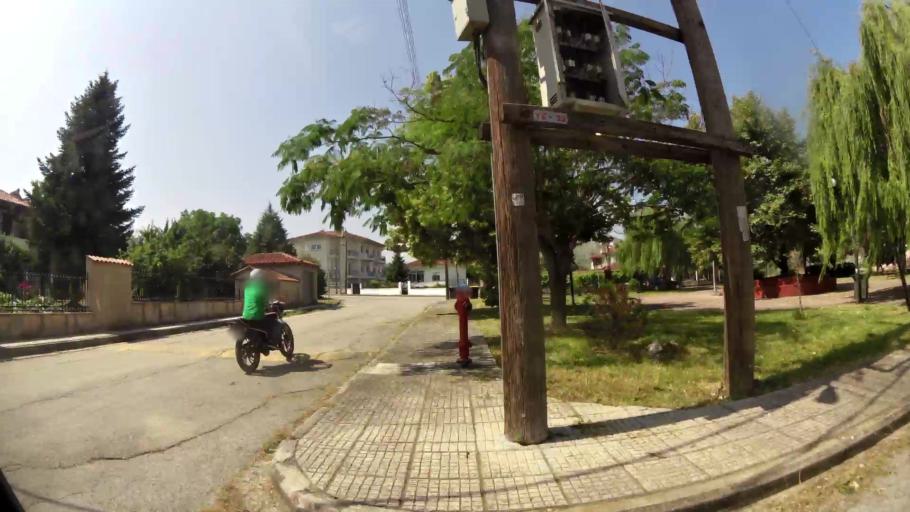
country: GR
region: West Macedonia
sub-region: Nomos Kozanis
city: Koila
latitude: 40.3304
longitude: 21.7880
